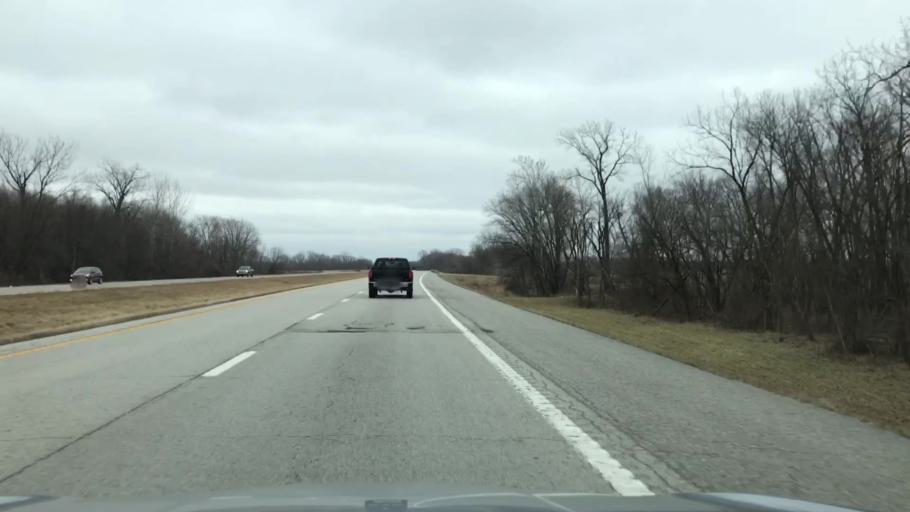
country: US
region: Missouri
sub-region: Livingston County
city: Chillicothe
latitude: 39.7768
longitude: -93.4385
